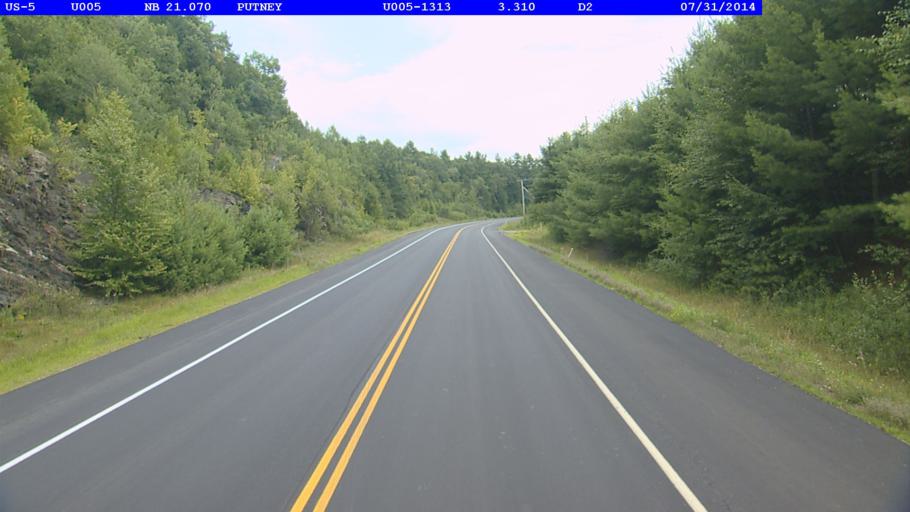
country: US
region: New Hampshire
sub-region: Cheshire County
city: Westmoreland
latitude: 42.9998
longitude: -72.4863
